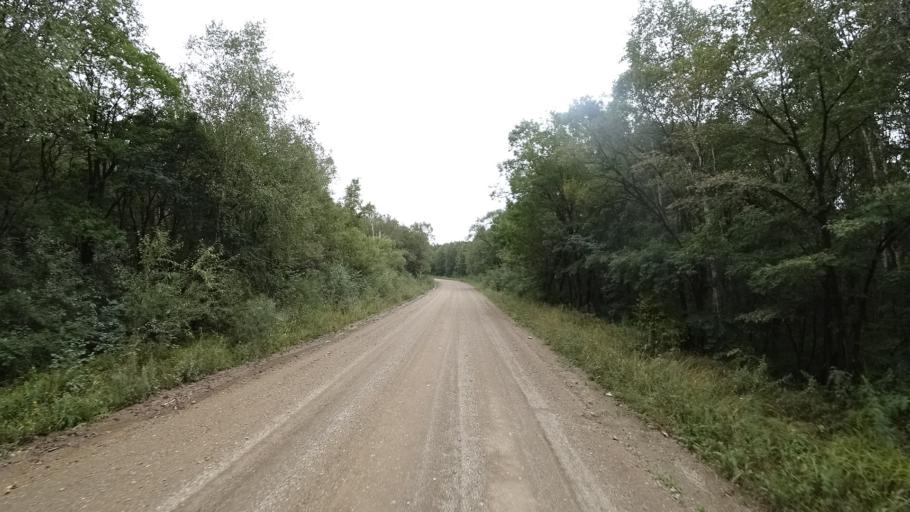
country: RU
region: Primorskiy
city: Ivanovka
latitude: 44.0408
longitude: 132.4956
